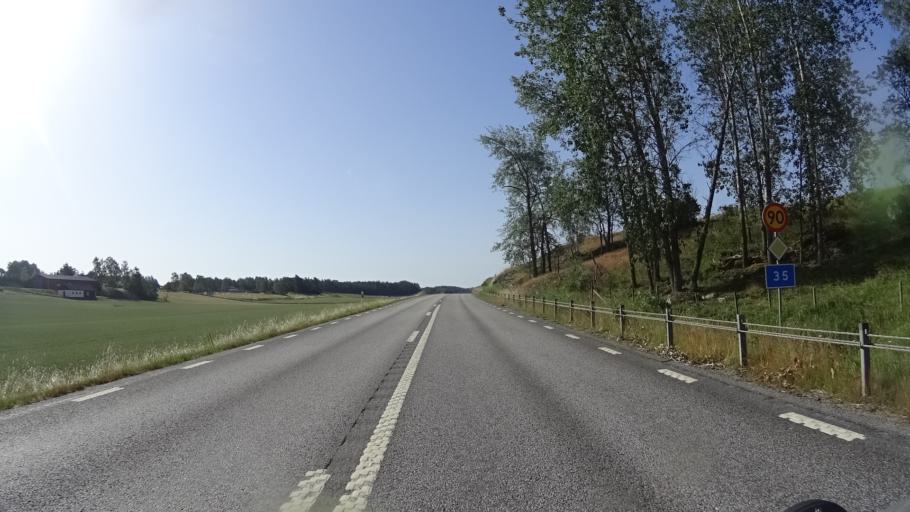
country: SE
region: OEstergoetland
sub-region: Linkopings Kommun
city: Linghem
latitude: 58.3479
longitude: 15.8401
